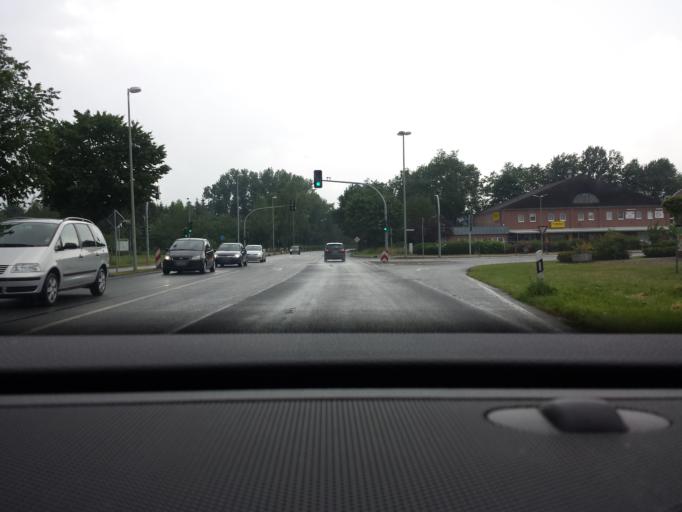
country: DE
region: North Rhine-Westphalia
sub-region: Regierungsbezirk Munster
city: Ahaus
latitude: 52.0677
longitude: 7.0100
